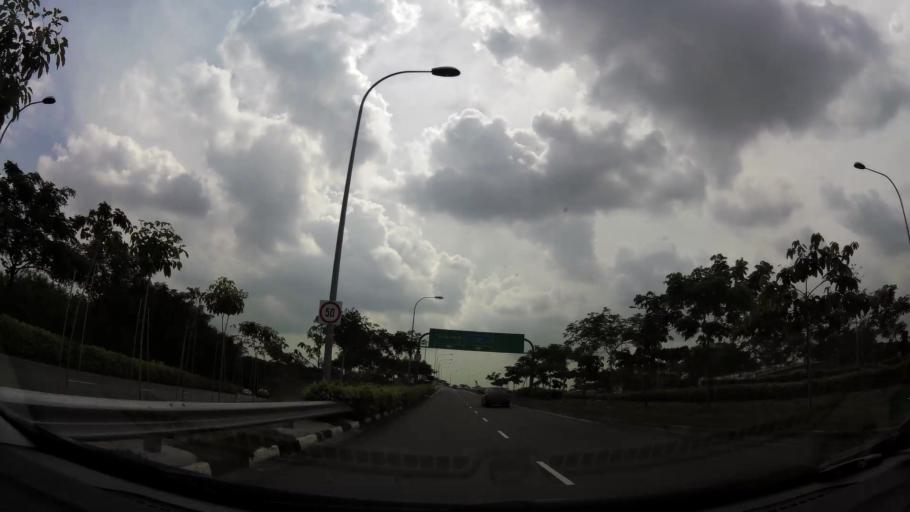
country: MY
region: Johor
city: Kampung Pasir Gudang Baru
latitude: 1.4010
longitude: 103.8561
